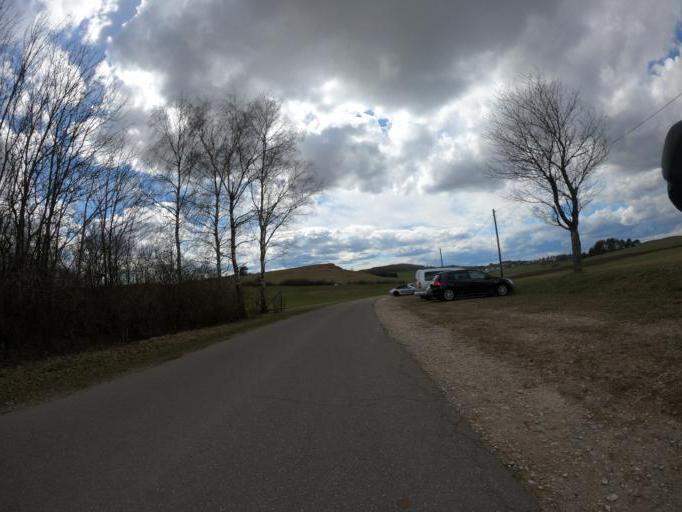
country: DE
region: Baden-Wuerttemberg
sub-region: Tuebingen Region
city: Pfullingen
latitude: 48.3875
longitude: 9.2108
